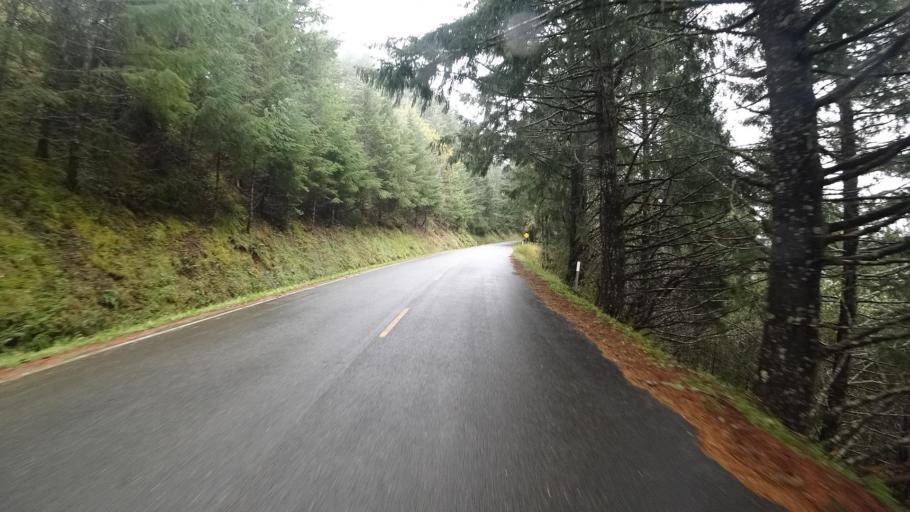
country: US
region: California
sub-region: Humboldt County
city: Westhaven-Moonstone
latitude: 41.1422
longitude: -123.8547
